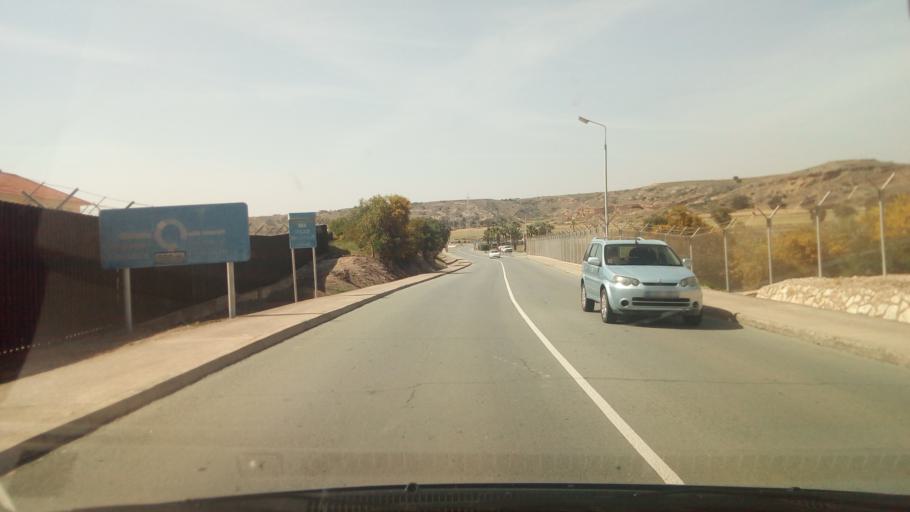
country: CY
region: Larnaka
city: Xylotymbou
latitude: 34.9830
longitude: 33.7214
